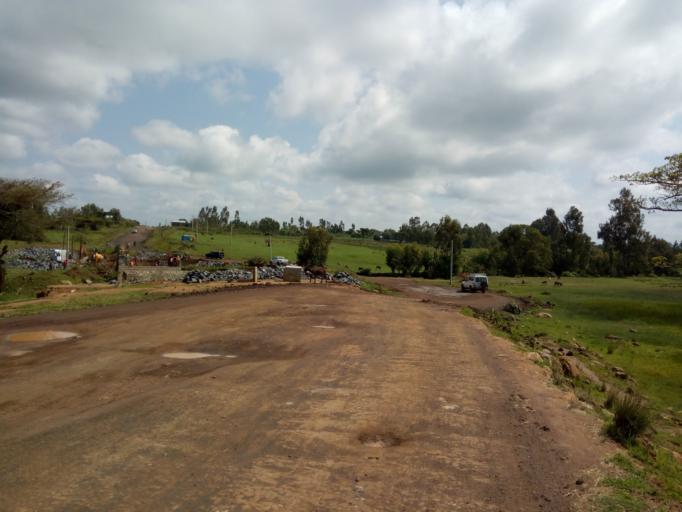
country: ET
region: Oromiya
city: Waliso
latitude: 8.5625
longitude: 37.9472
